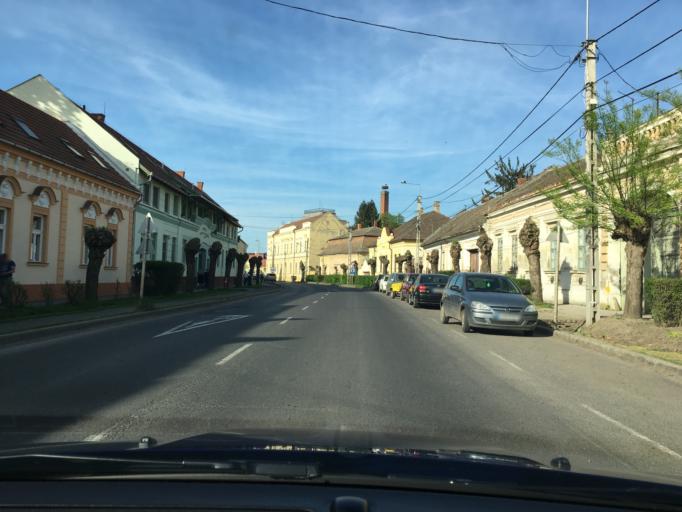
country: HU
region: Bekes
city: Mezobereny
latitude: 46.8223
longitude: 21.0280
